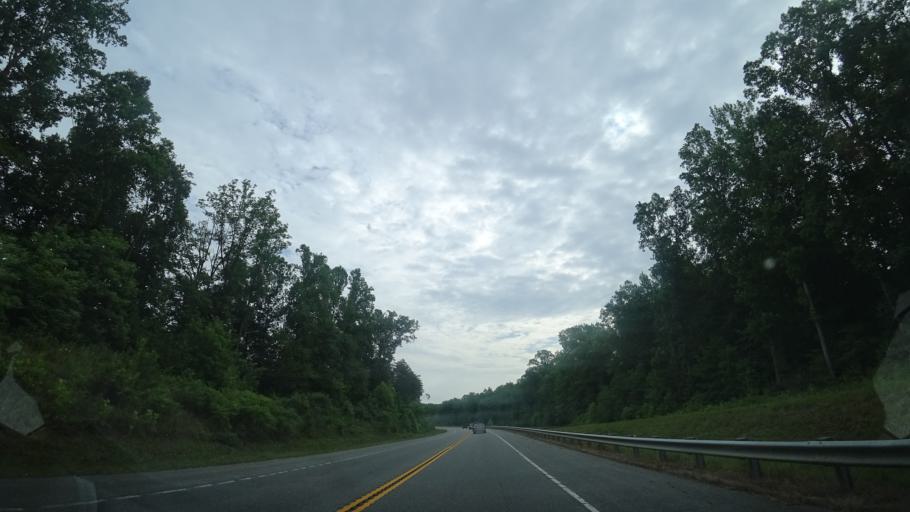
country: US
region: Virginia
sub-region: Spotsylvania County
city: Spotsylvania Courthouse
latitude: 38.1765
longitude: -77.6280
